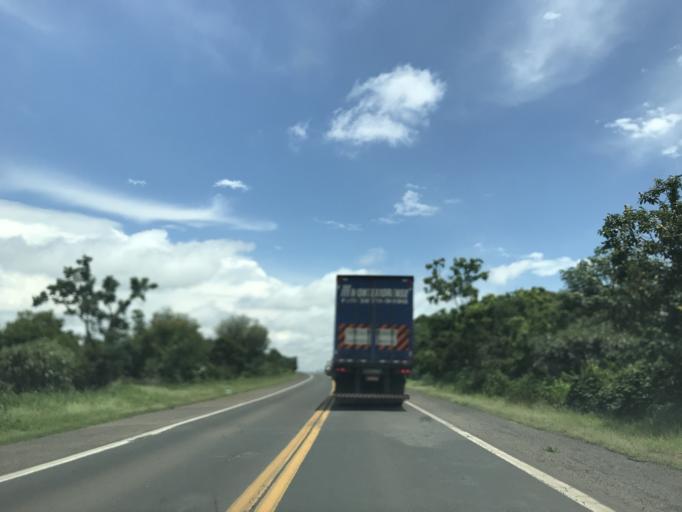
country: BR
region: Minas Gerais
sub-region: Prata
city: Prata
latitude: -19.6556
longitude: -48.9764
